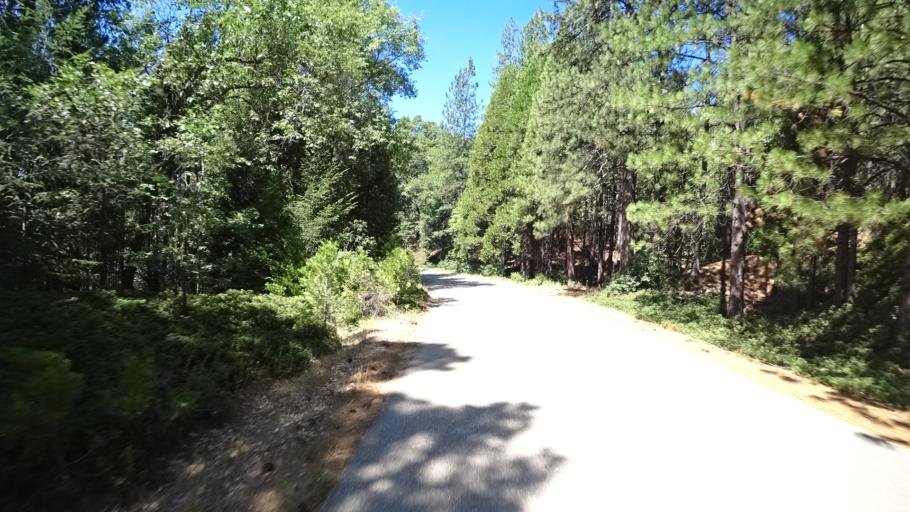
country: US
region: California
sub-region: Amador County
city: Pioneer
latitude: 38.4277
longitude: -120.4807
